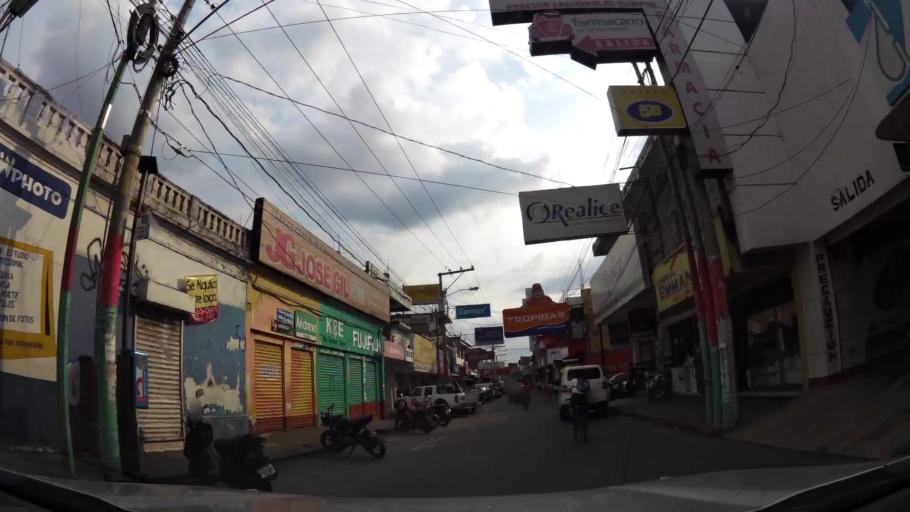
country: GT
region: Escuintla
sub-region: Municipio de Escuintla
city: Escuintla
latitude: 14.3043
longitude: -90.7845
